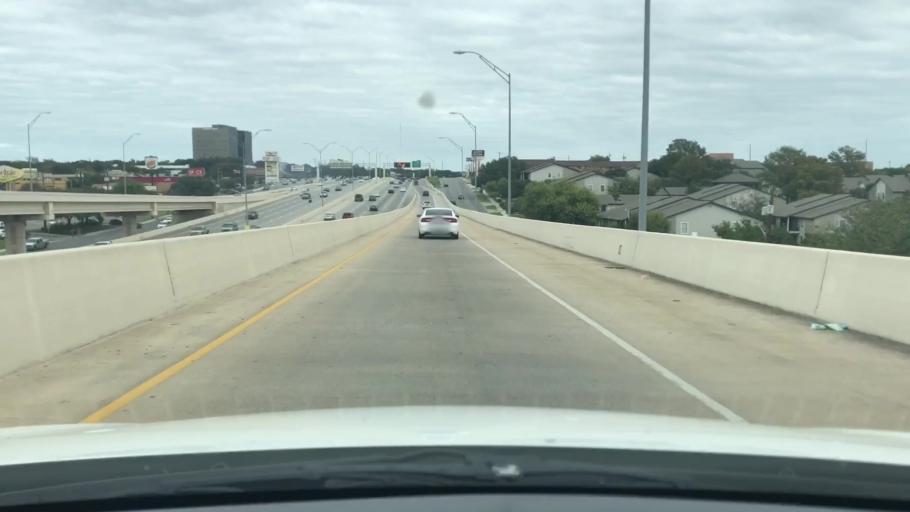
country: US
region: Texas
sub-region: Bexar County
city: Leon Valley
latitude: 29.4867
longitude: -98.5877
